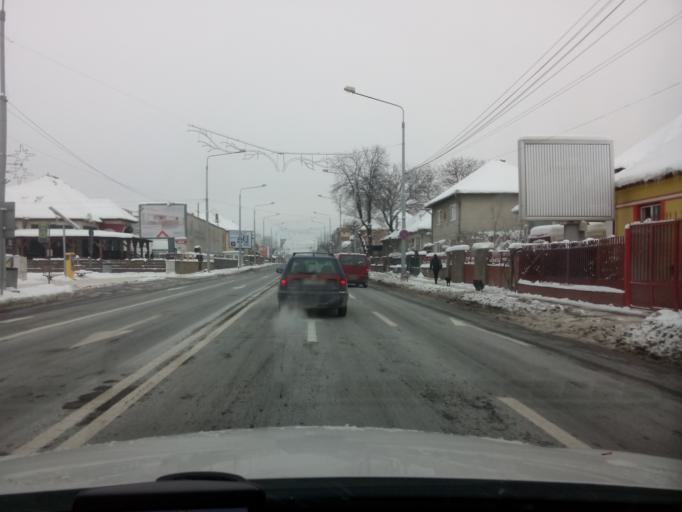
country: RO
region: Sibiu
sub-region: Municipiul Sibiu
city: Sibiu
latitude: 45.7846
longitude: 24.1614
